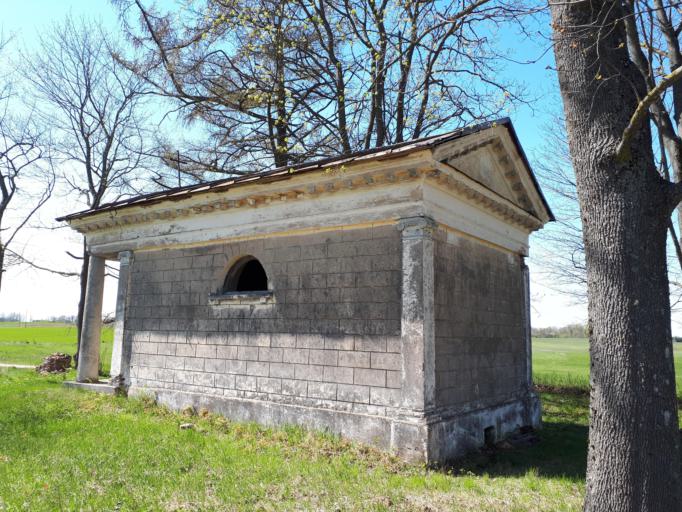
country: LT
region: Vilnius County
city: Ukmerge
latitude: 55.1481
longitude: 24.7269
